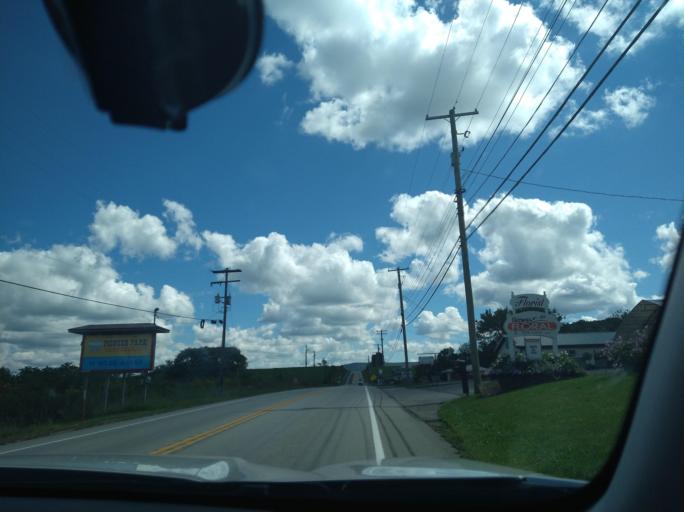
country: US
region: Pennsylvania
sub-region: Fayette County
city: Bear Rocks
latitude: 40.1054
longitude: -79.3728
